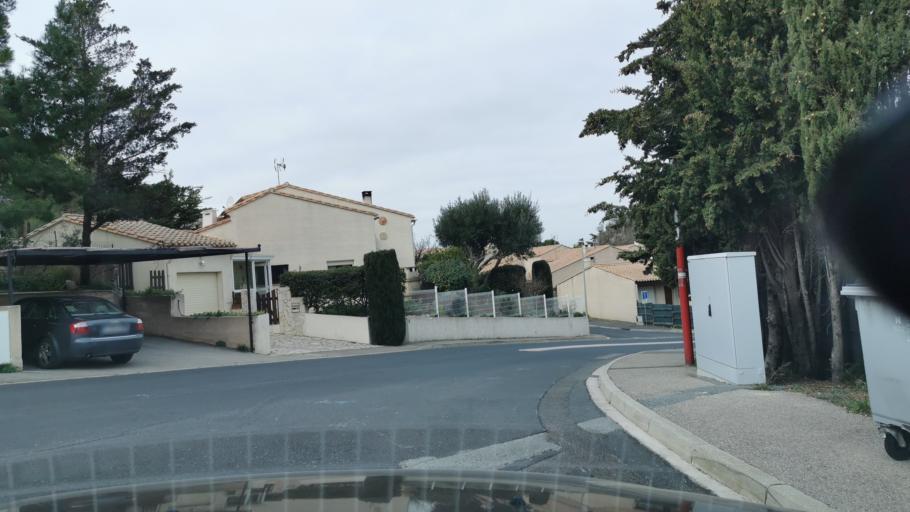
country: FR
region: Languedoc-Roussillon
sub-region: Departement de l'Aude
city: Narbonne
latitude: 43.1659
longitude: 2.9775
